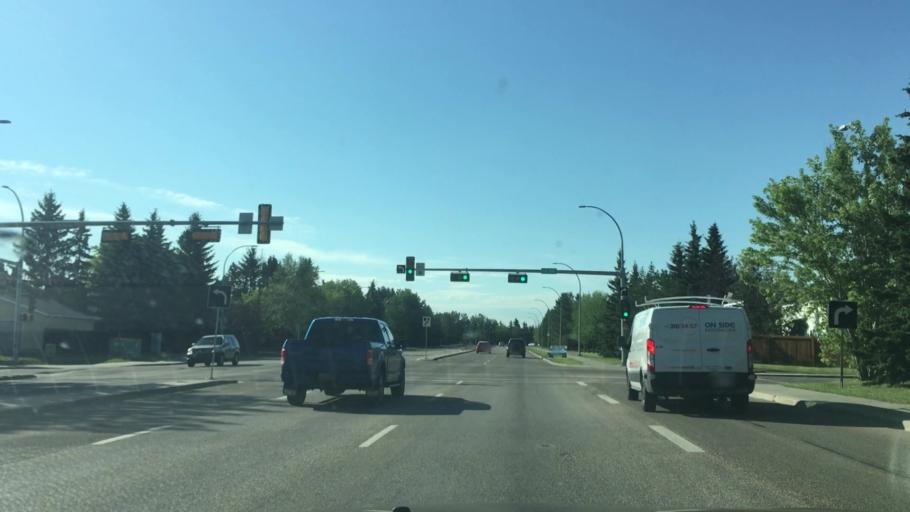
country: CA
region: Alberta
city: Edmonton
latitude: 53.4595
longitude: -113.5379
